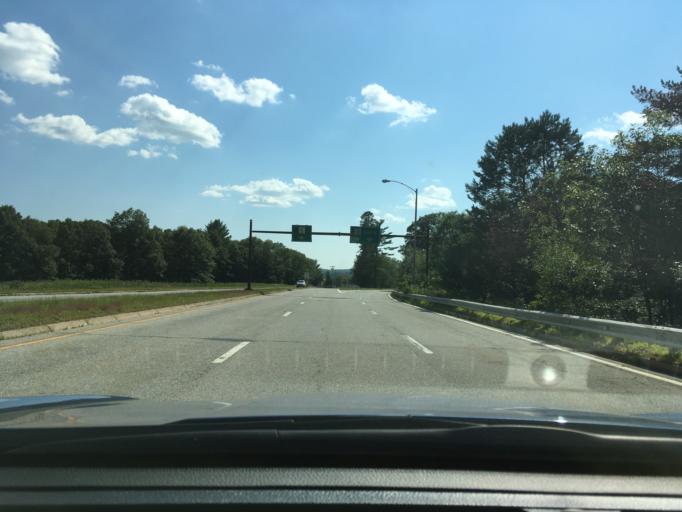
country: US
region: Rhode Island
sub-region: Providence County
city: Cranston
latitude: 41.7420
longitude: -71.4738
